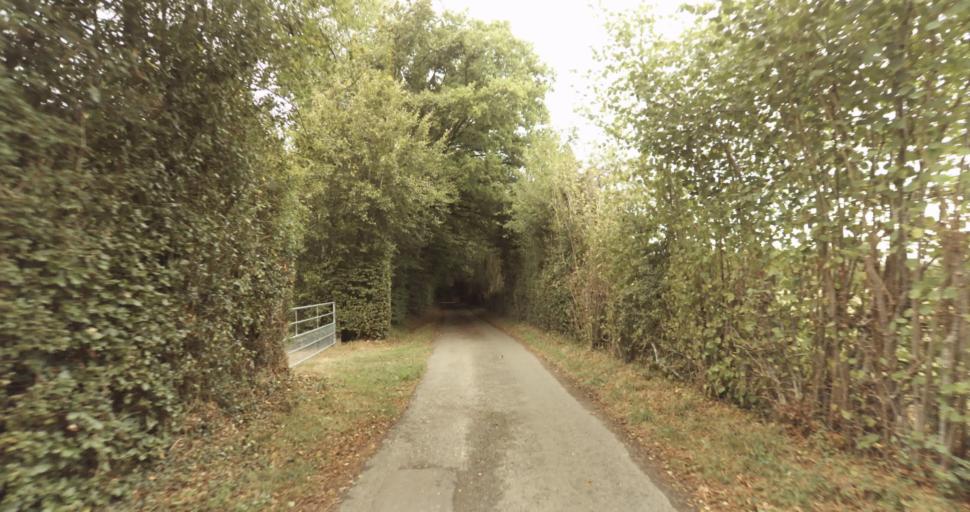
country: FR
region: Lower Normandy
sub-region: Departement de l'Orne
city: Gace
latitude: 48.8621
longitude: 0.3165
